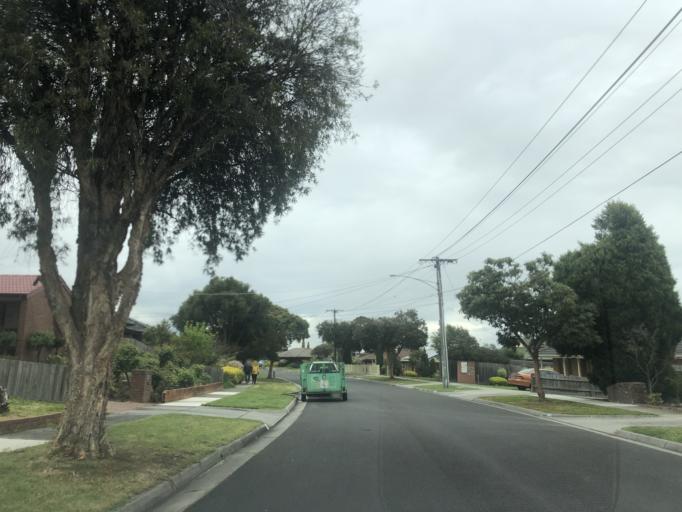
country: AU
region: Victoria
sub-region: Greater Dandenong
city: Dandenong North
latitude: -37.9617
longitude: 145.2189
